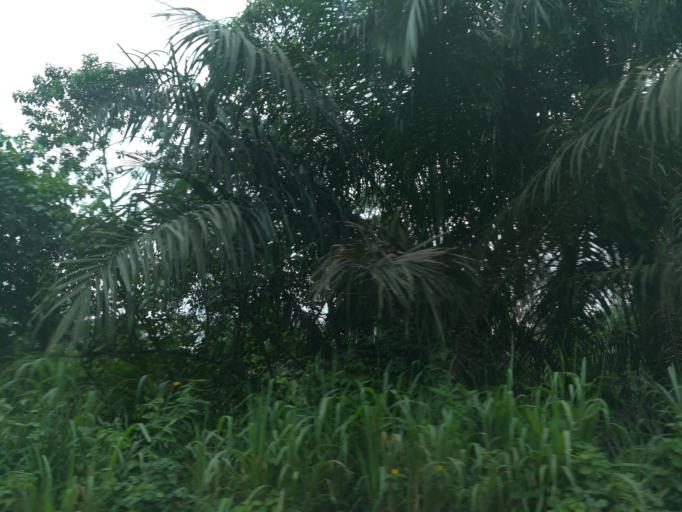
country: NG
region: Lagos
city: Ejirin
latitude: 6.6605
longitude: 3.8157
